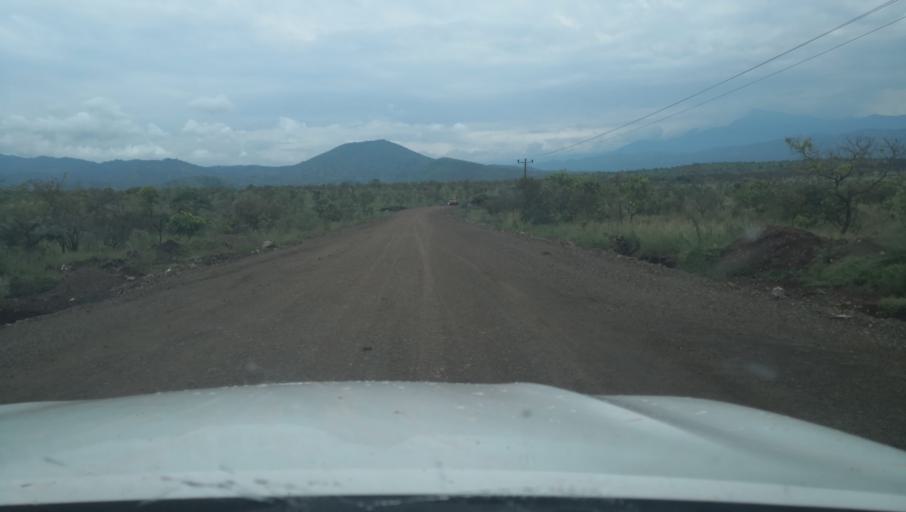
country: ET
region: Southern Nations, Nationalities, and People's Region
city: Felege Neway
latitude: 6.4239
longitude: 37.2423
